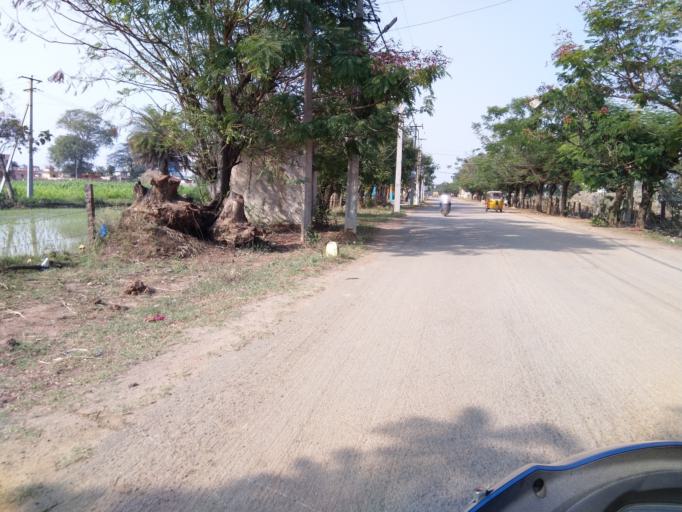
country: IN
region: Telangana
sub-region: Rangareddi
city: Quthbullapur
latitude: 17.5888
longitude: 78.4186
